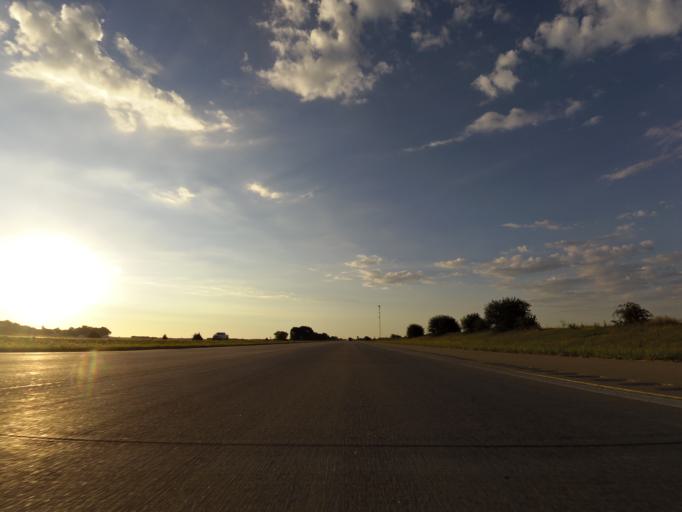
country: US
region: Kansas
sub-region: Reno County
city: Haven
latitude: 37.9153
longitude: -97.8199
